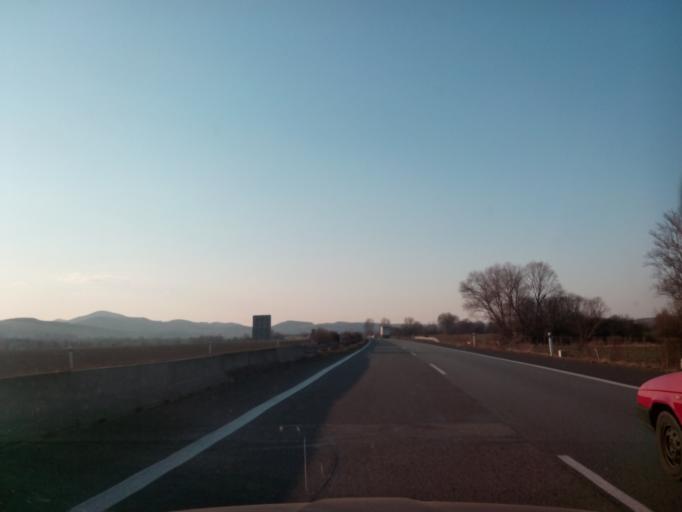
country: SK
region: Kosicky
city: Kosice
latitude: 48.8399
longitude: 21.3000
